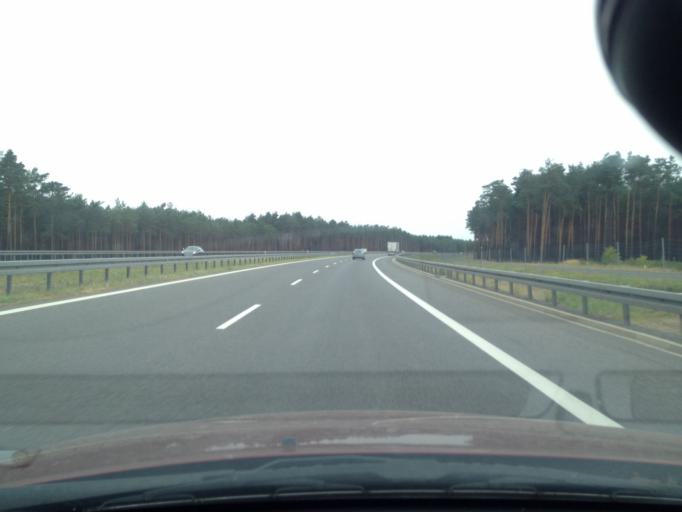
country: PL
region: Lubusz
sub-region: Powiat gorzowski
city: Deszczno
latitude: 52.6166
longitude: 15.3912
